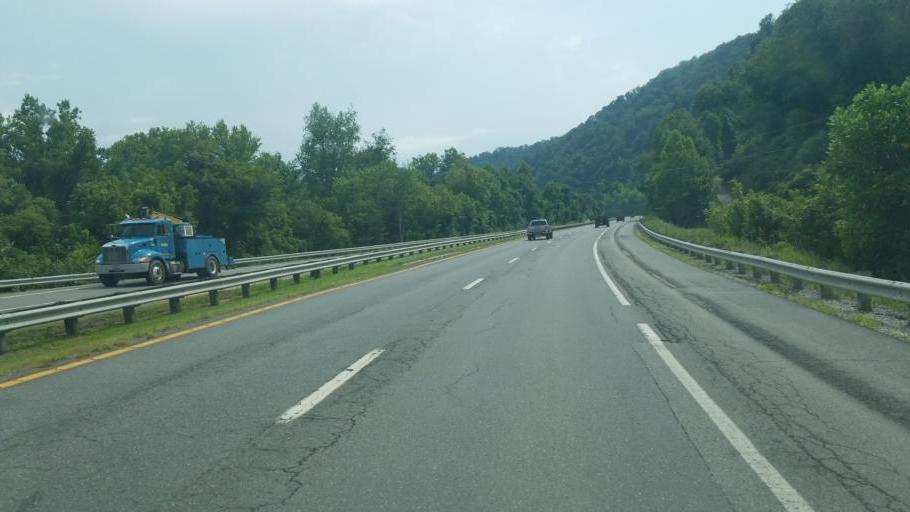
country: US
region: West Virginia
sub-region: Logan County
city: Chapmanville
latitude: 37.9518
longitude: -82.0165
